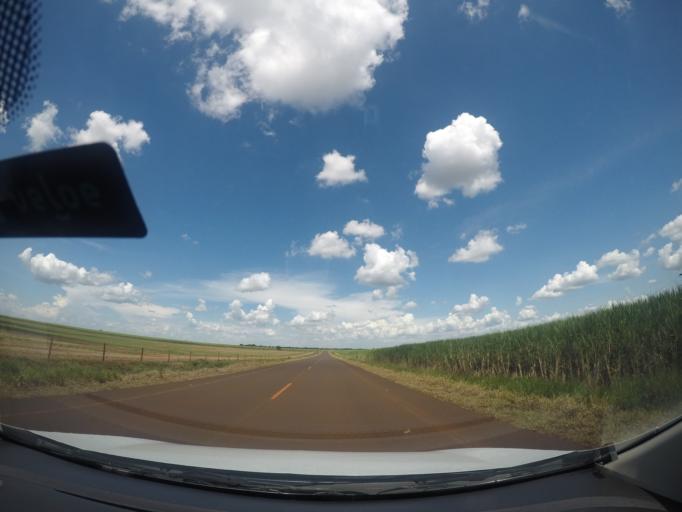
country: BR
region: Minas Gerais
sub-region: Conceicao Das Alagoas
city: Conceicao das Alagoas
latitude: -19.9236
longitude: -48.6724
